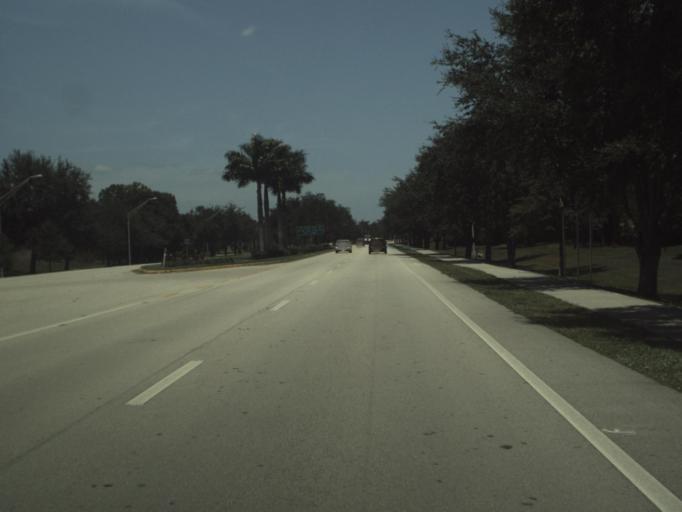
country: US
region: Florida
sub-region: Martin County
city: Palm City
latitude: 27.1664
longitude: -80.2998
